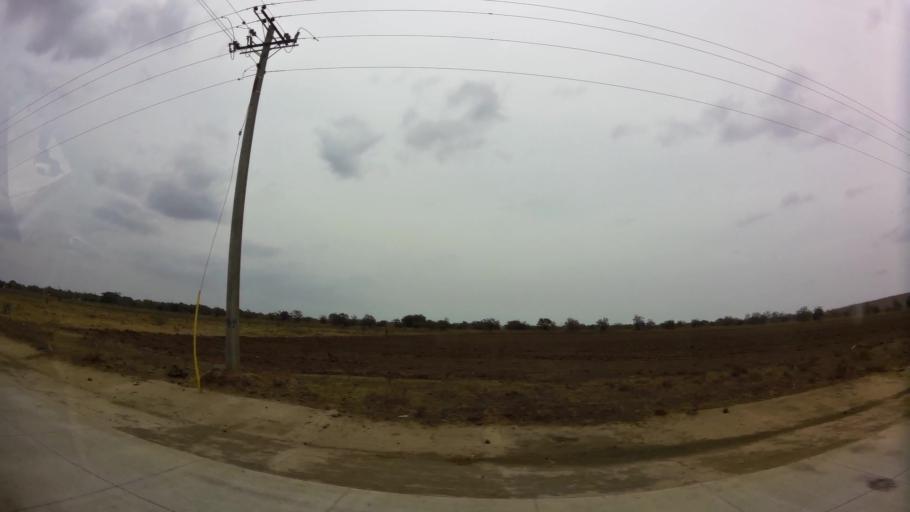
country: NI
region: Managua
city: Managua
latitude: 12.1103
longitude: -86.1735
